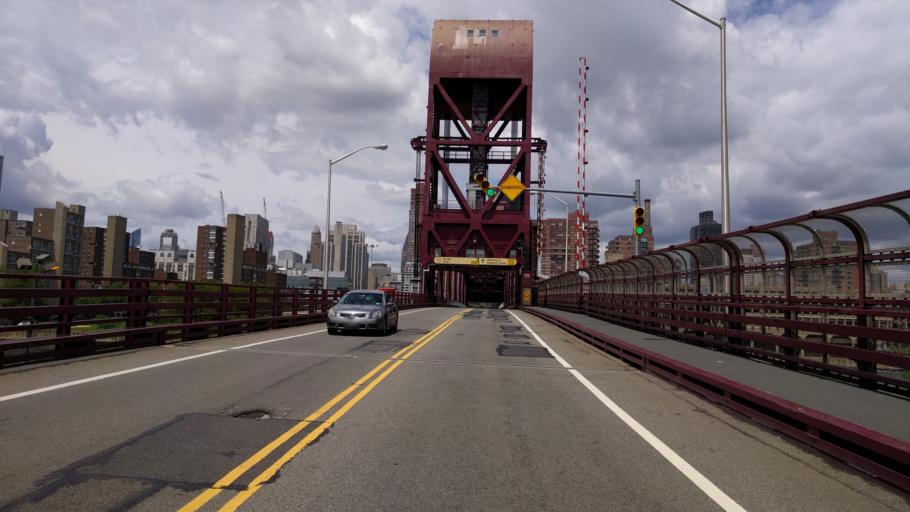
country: US
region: New York
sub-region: Queens County
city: Long Island City
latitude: 40.7627
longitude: -73.9442
